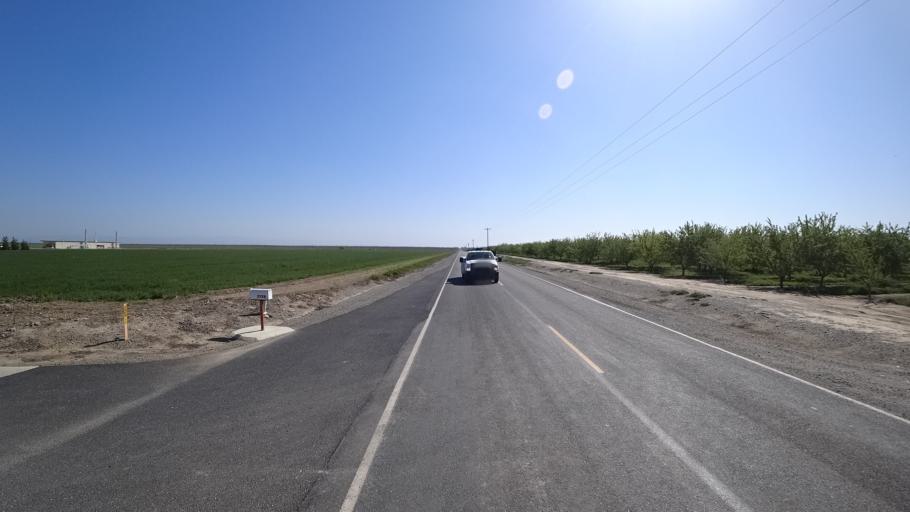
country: US
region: California
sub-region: Glenn County
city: Hamilton City
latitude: 39.6597
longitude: -122.0554
